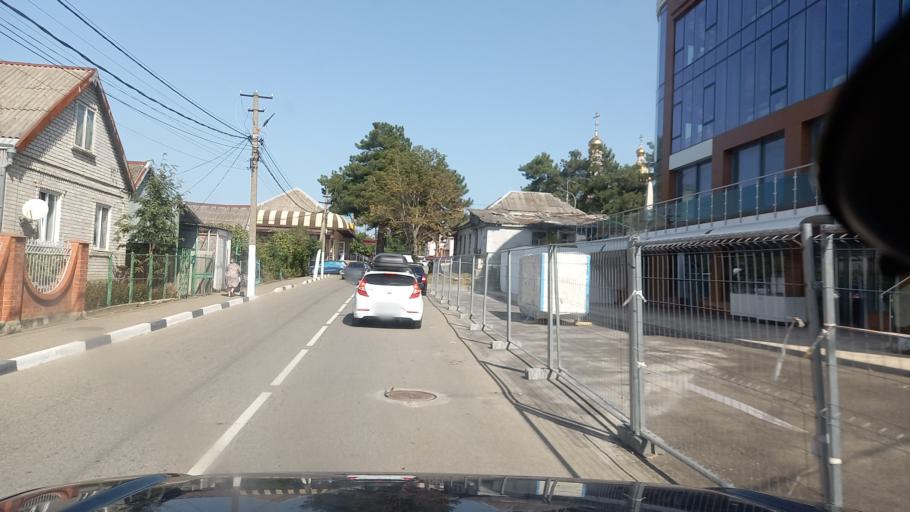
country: RU
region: Krasnodarskiy
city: Arkhipo-Osipovka
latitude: 44.3696
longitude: 38.5327
